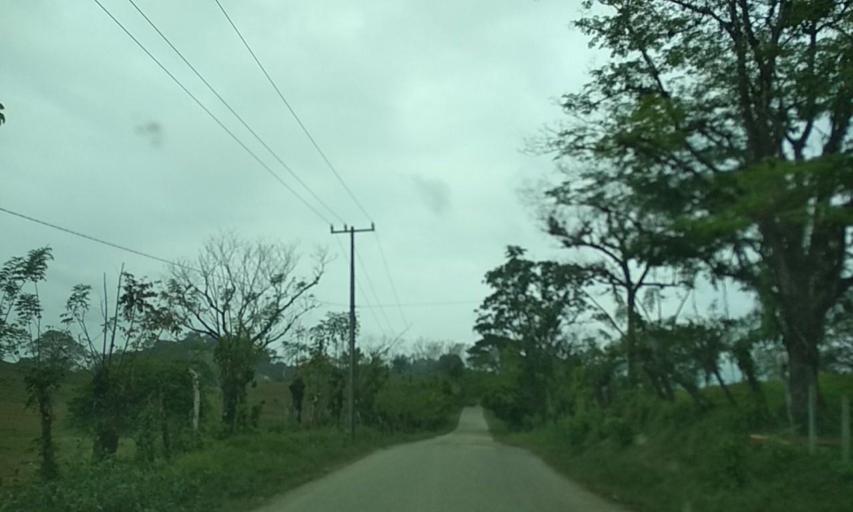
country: MX
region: Veracruz
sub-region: Uxpanapa
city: Poblado 10
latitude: 17.4813
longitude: -94.1244
